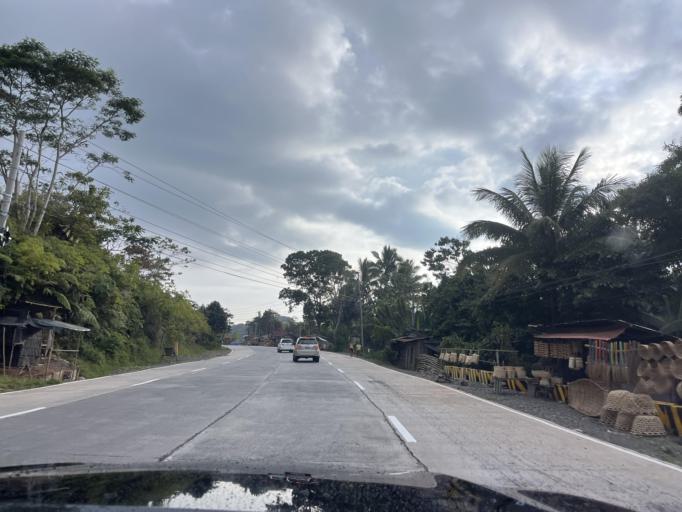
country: PH
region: Northern Mindanao
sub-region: Province of Bukidnon
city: Dalorong
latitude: 7.5697
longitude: 125.2134
